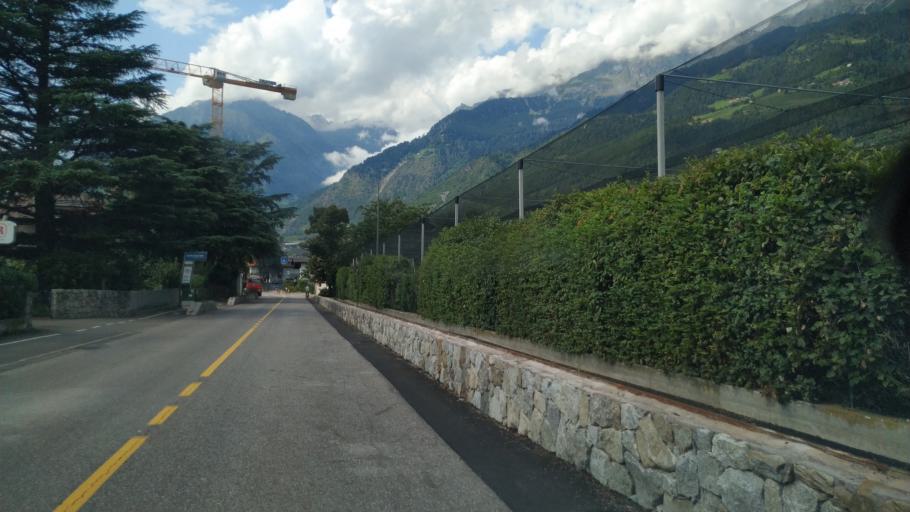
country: IT
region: Trentino-Alto Adige
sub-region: Bolzano
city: Lagundo
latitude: 46.6793
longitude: 11.1371
